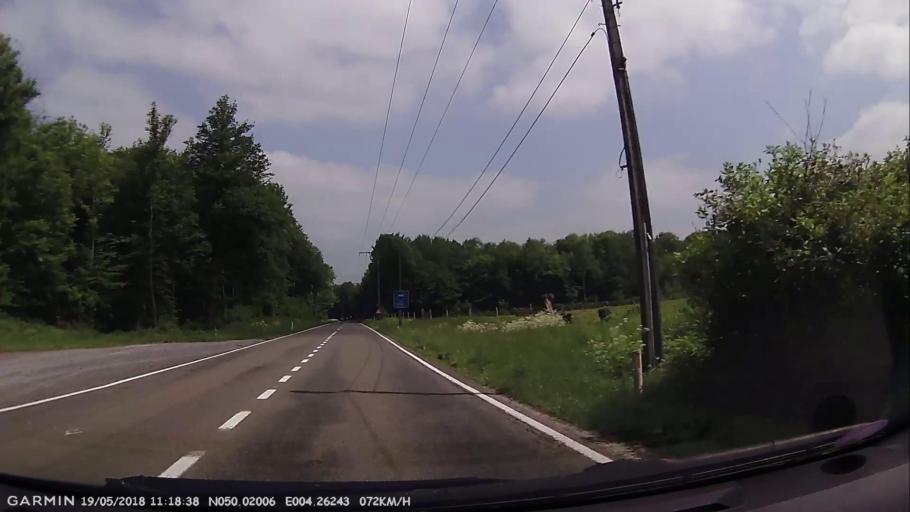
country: BE
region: Wallonia
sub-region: Province du Hainaut
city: Chimay
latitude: 50.0201
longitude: 4.2629
